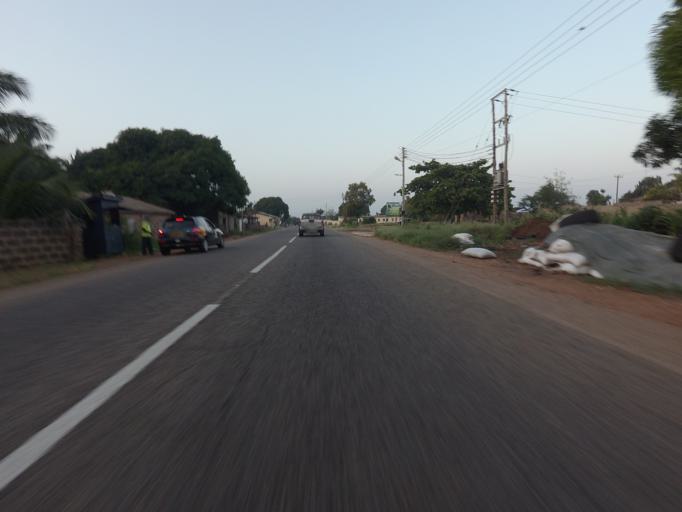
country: GH
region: Volta
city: Anloga
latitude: 5.8258
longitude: 0.9493
